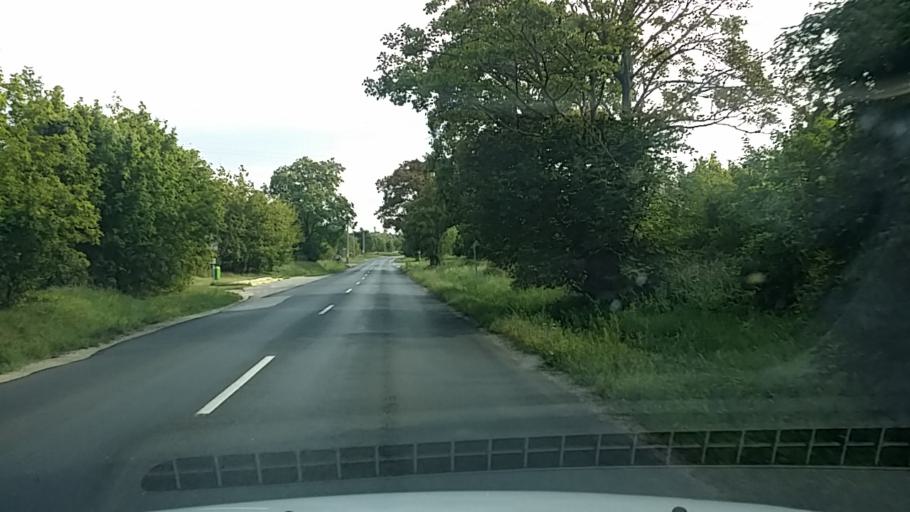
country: HU
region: Gyor-Moson-Sopron
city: Sopron
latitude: 47.7013
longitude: 16.6056
